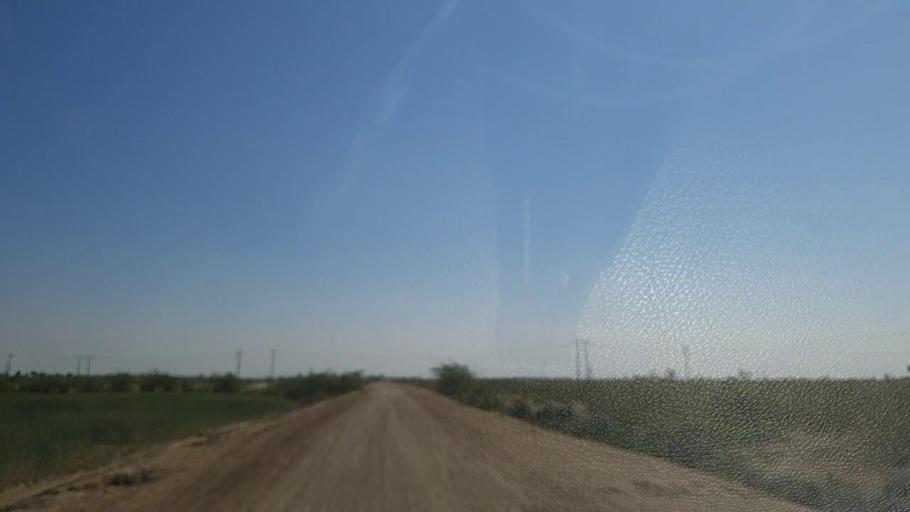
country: PK
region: Sindh
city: Samaro
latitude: 25.3058
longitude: 69.4795
